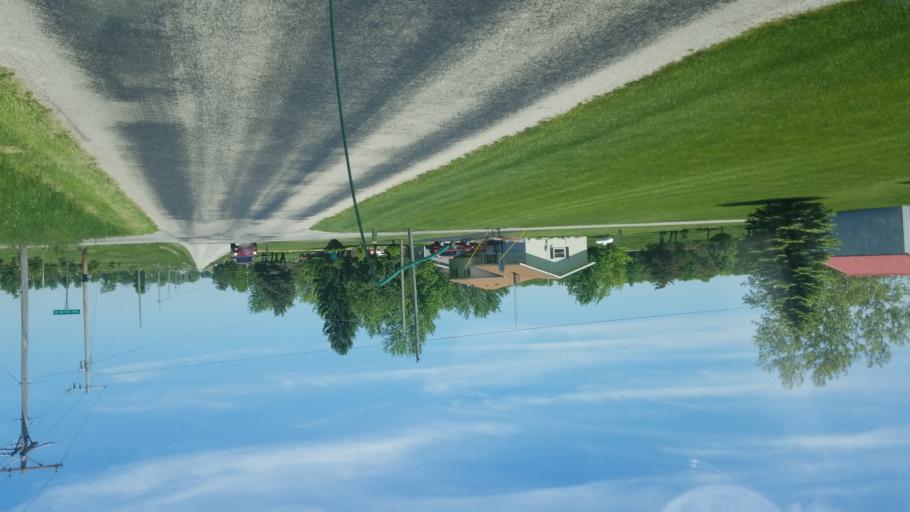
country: US
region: Ohio
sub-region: Huron County
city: Greenwich
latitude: 41.1392
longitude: -82.5383
